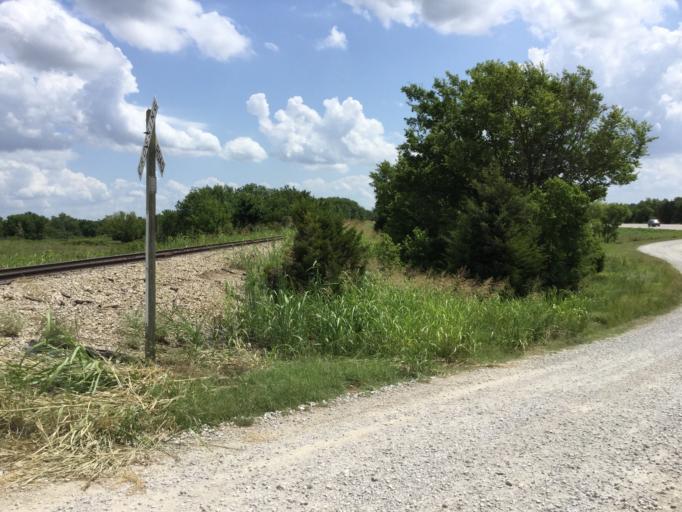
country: US
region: Kansas
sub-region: Montgomery County
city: Caney
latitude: 37.1106
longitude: -95.9048
